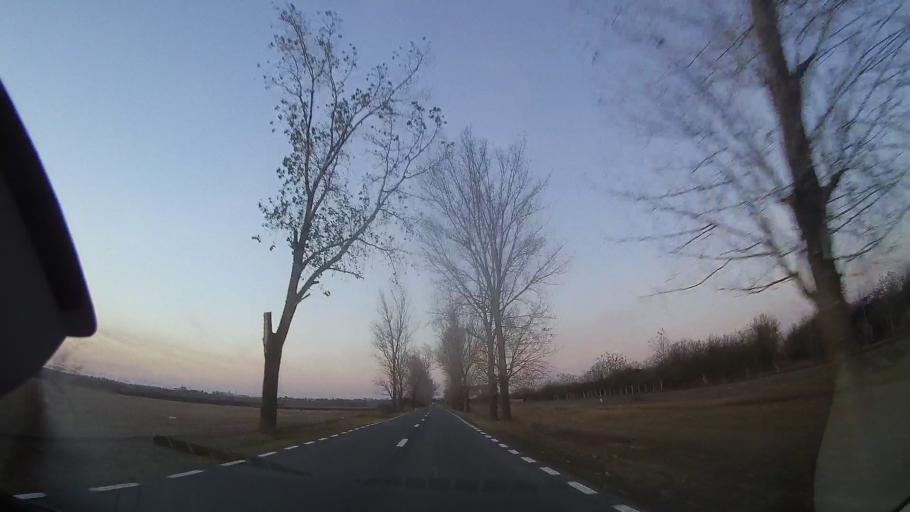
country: RO
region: Constanta
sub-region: Comuna Cobadin
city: Cobadin
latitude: 44.0446
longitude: 28.2537
